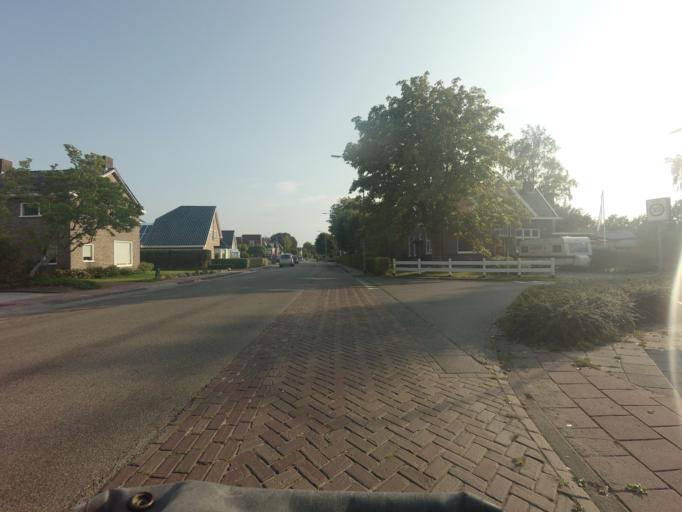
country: NL
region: Groningen
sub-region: Gemeente Haren
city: Haren
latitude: 53.1379
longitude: 6.5643
